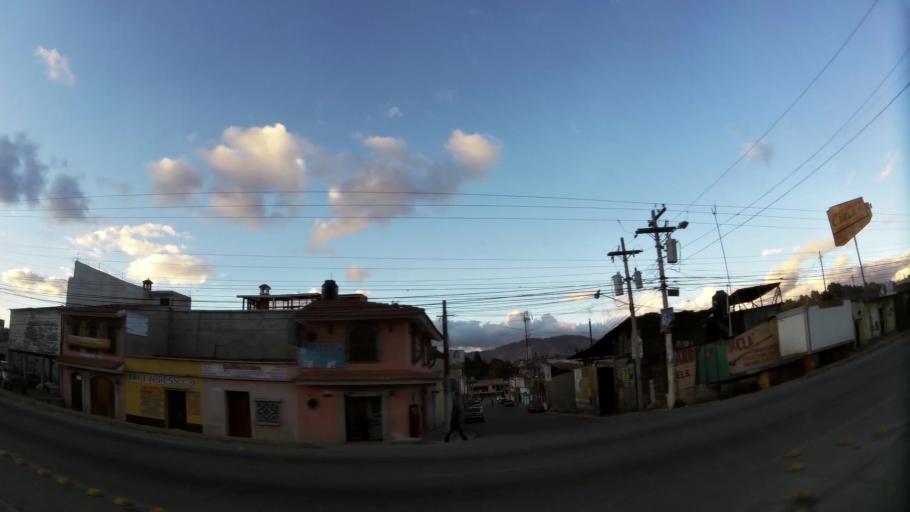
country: GT
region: Quetzaltenango
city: Quetzaltenango
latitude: 14.8401
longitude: -91.5020
